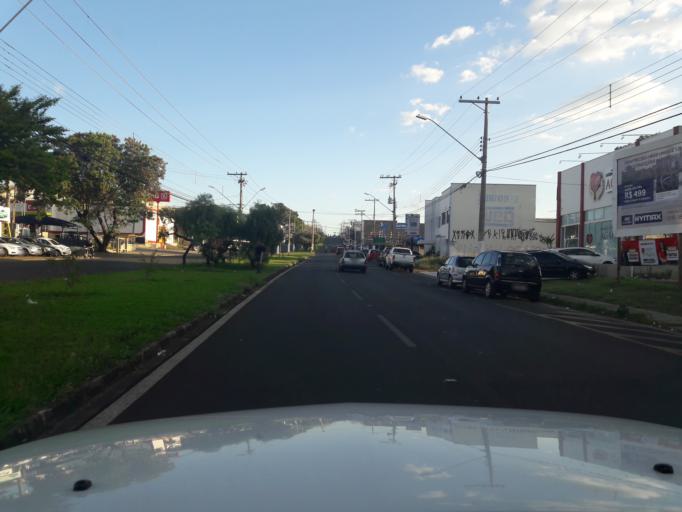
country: BR
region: Sao Paulo
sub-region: Moji-Guacu
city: Mogi-Gaucu
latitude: -22.3857
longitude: -46.9435
